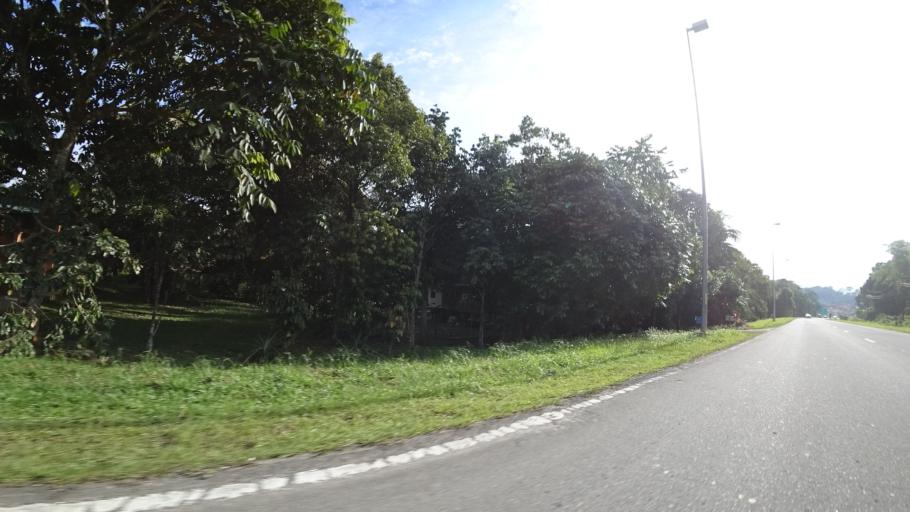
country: MY
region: Sarawak
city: Limbang
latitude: 4.7692
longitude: 114.8283
